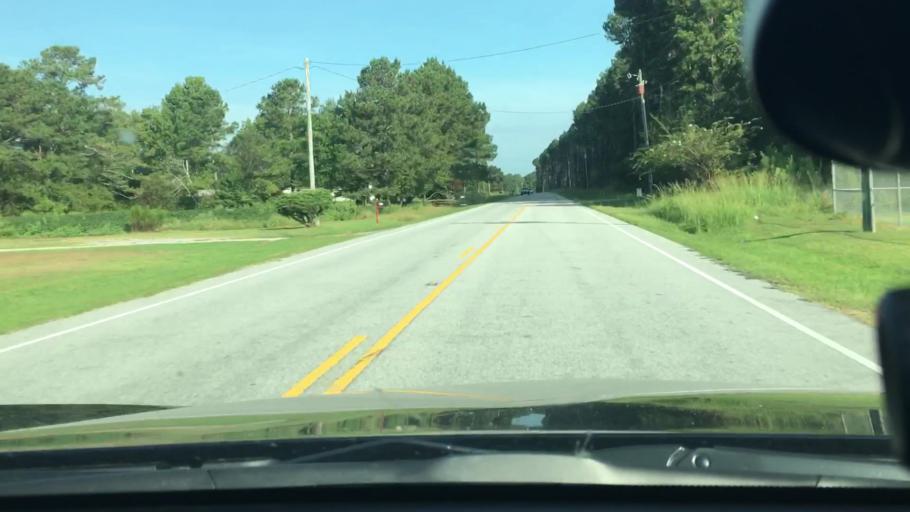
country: US
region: North Carolina
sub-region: Pitt County
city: Farmville
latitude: 35.7123
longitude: -77.5225
